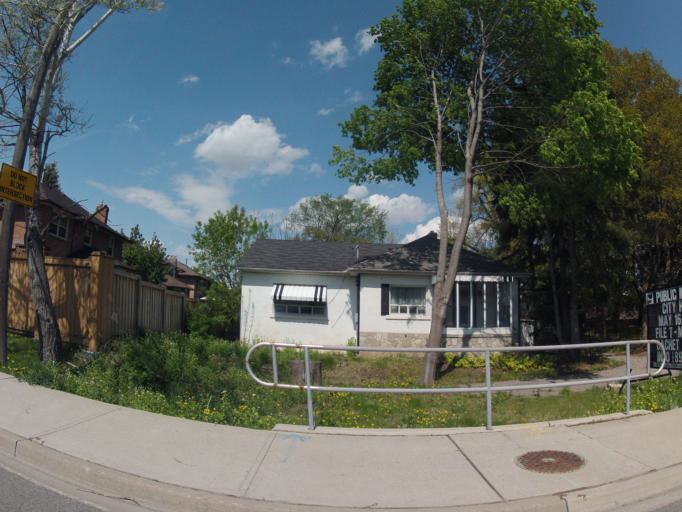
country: CA
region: Ontario
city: Mississauga
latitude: 43.5726
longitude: -79.7013
